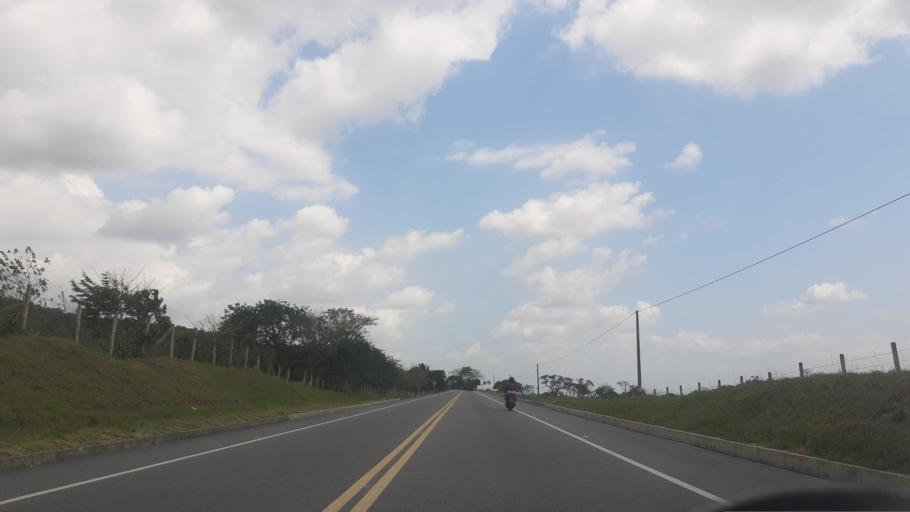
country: CO
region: Casanare
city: Tauramena
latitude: 4.8612
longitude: -72.7159
